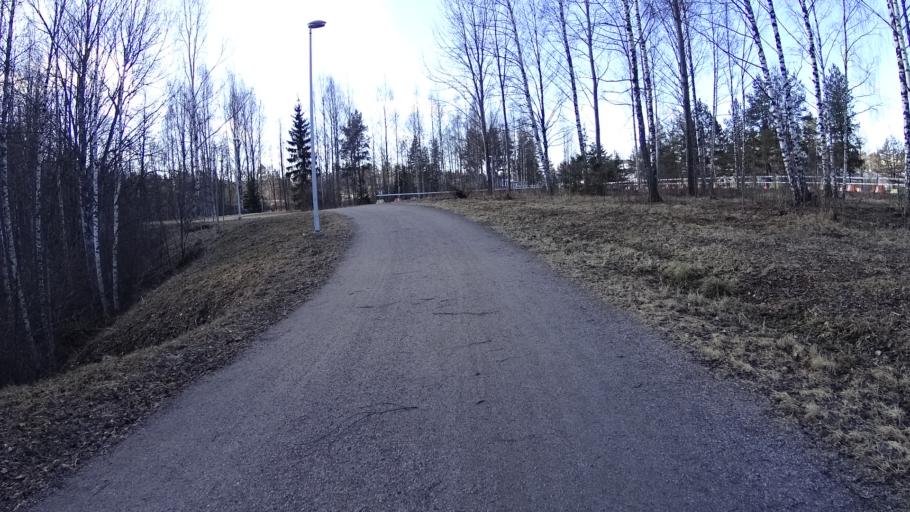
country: FI
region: Uusimaa
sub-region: Helsinki
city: Teekkarikylae
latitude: 60.2723
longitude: 24.8798
